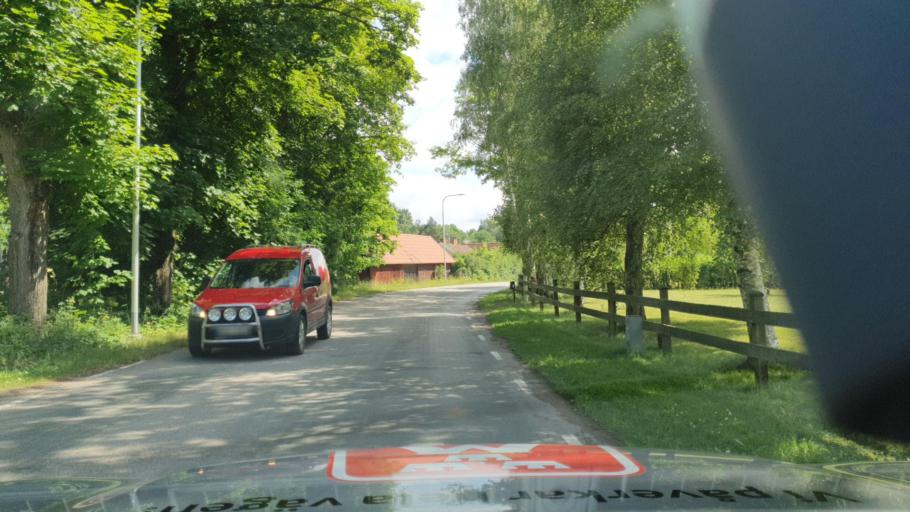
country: SE
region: Kalmar
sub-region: Kalmar Kommun
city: Ljungbyholm
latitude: 56.5472
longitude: 16.1838
